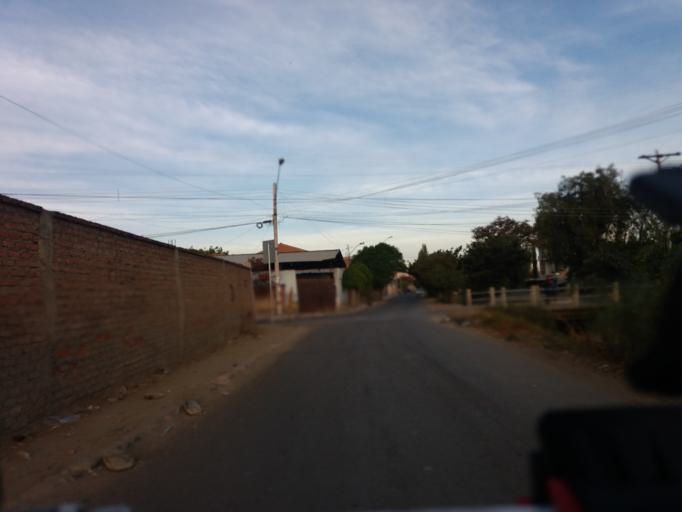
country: BO
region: Cochabamba
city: Cochabamba
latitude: -17.3590
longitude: -66.1905
